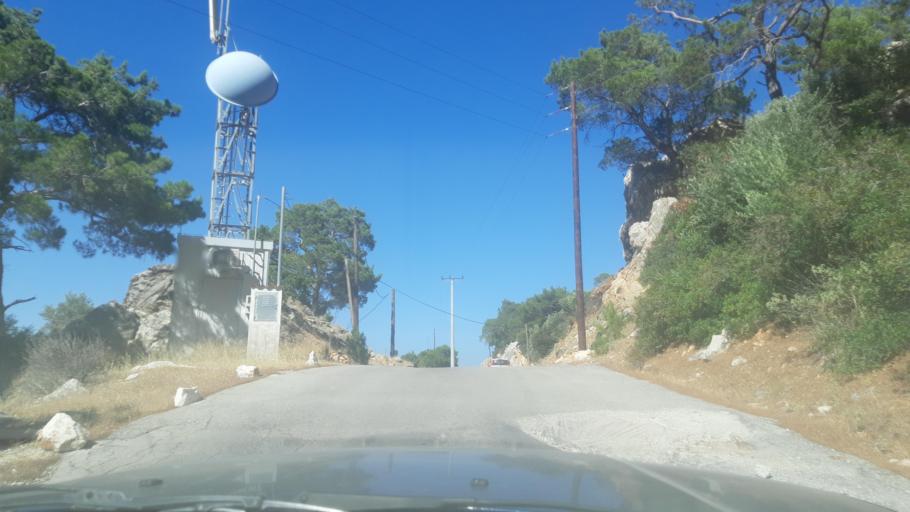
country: GR
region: South Aegean
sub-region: Nomos Dodekanisou
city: Karpathos
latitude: 35.5846
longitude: 27.1767
